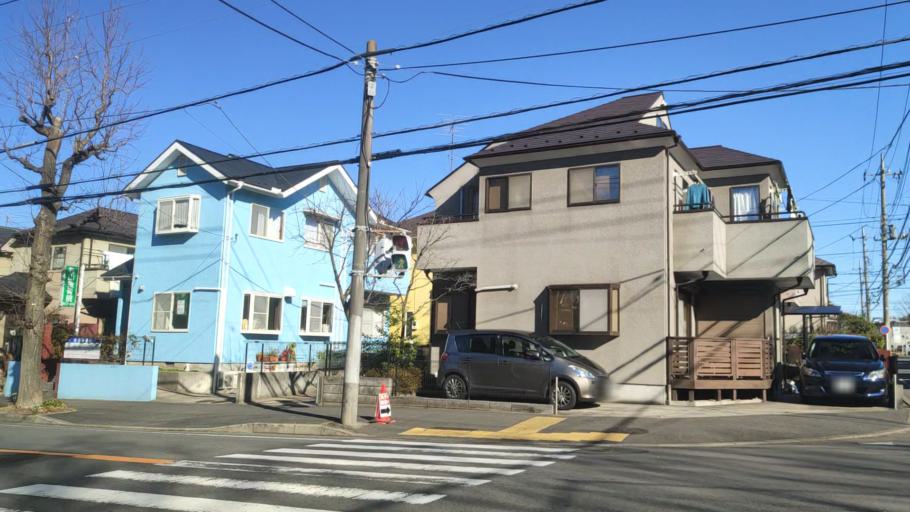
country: JP
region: Tokyo
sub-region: Machida-shi
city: Machida
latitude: 35.5112
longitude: 139.5029
